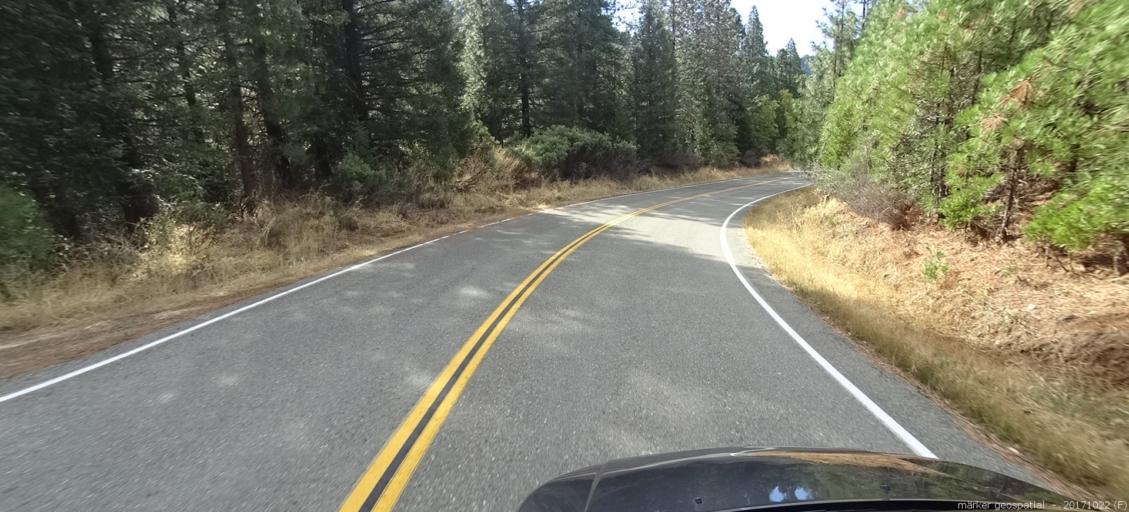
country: US
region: California
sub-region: Siskiyou County
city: Dunsmuir
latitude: 41.0606
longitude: -122.3715
